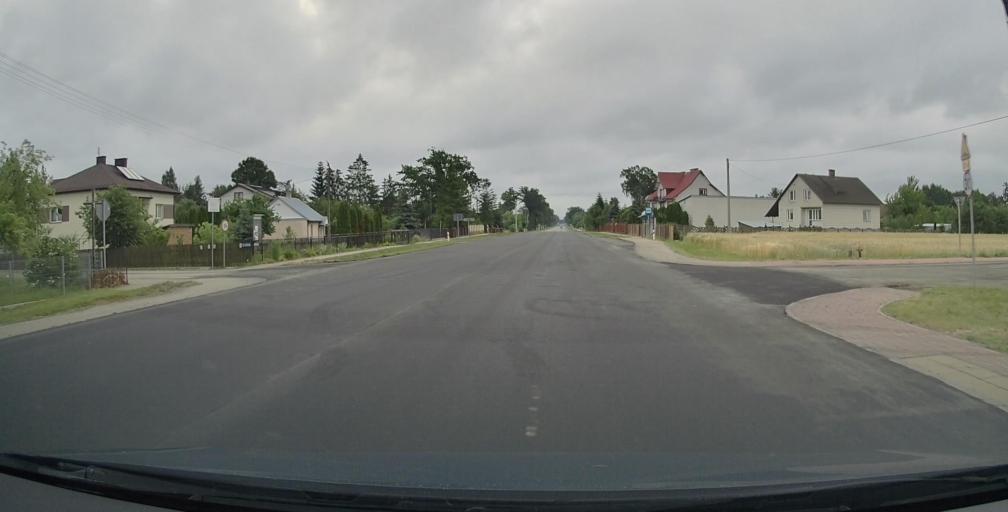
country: PL
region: Lublin Voivodeship
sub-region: Powiat lukowski
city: Trzebieszow
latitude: 52.0538
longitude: 22.6485
